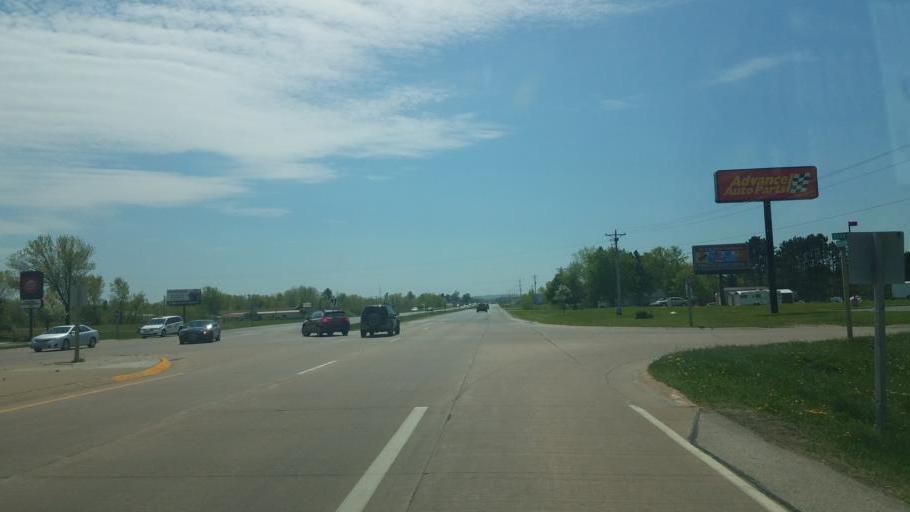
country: US
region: Wisconsin
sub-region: Monroe County
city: Tomah
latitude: 44.0164
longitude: -90.5057
